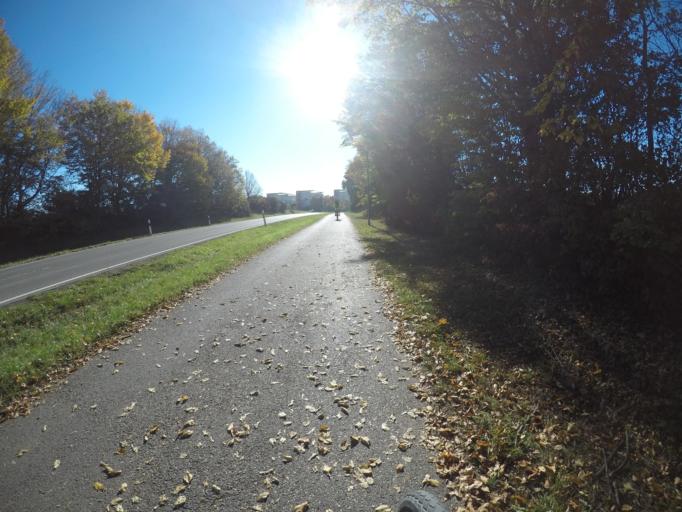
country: DE
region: Baden-Wuerttemberg
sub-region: Regierungsbezirk Stuttgart
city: Filderstadt
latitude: 48.6620
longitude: 9.2162
